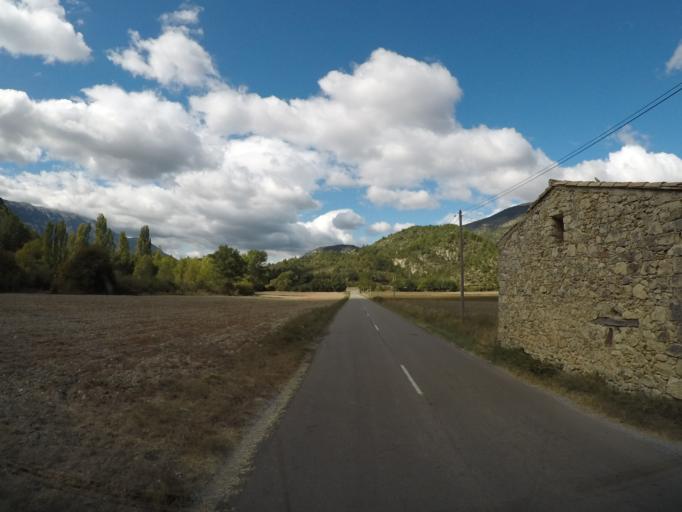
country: FR
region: Provence-Alpes-Cote d'Azur
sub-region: Departement du Vaucluse
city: Sault
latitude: 44.1814
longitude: 5.3914
